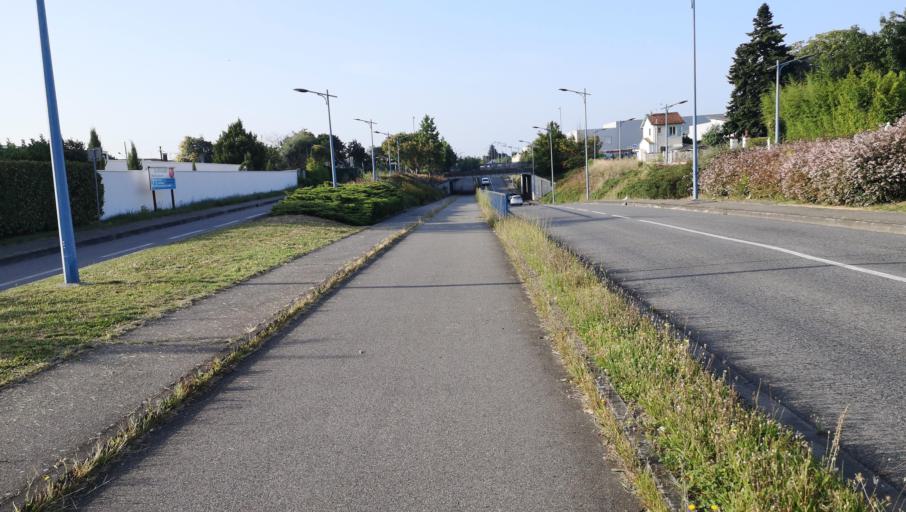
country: FR
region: Midi-Pyrenees
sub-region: Departement de la Haute-Garonne
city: Blagnac
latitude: 43.5977
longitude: 1.3930
